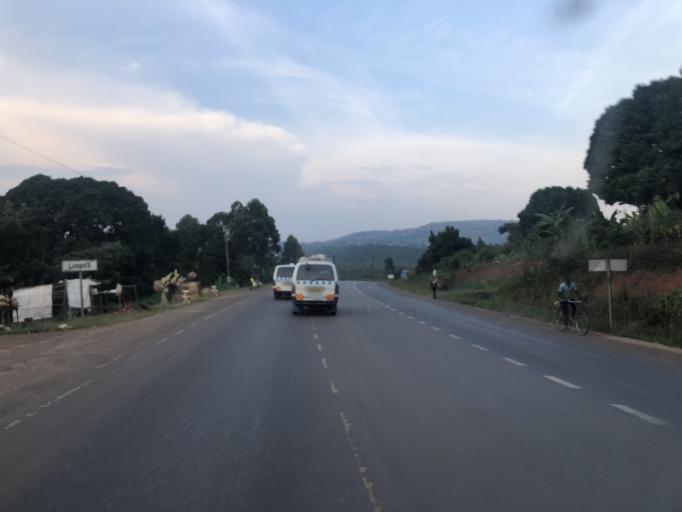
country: UG
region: Central Region
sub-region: Mpigi District
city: Mpigi
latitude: 0.2401
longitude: 32.3498
